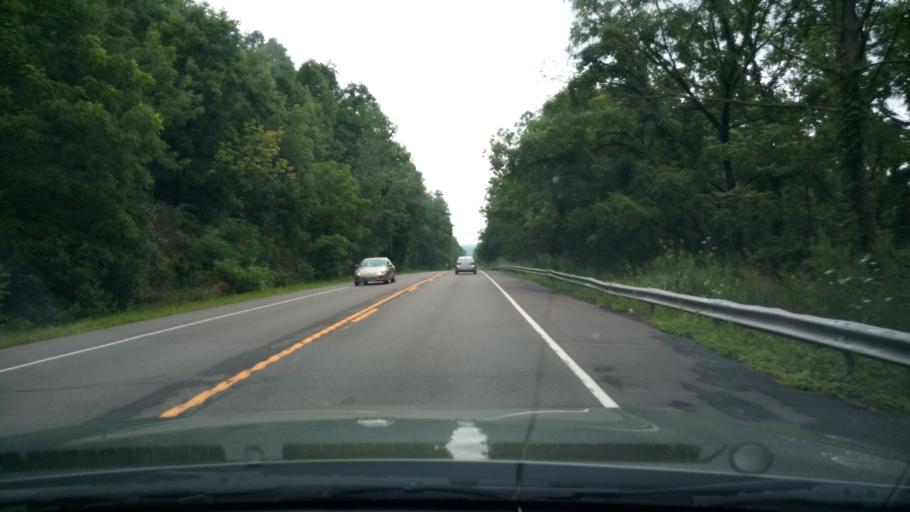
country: US
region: New York
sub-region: Tompkins County
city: South Hill
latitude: 42.3631
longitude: -76.5945
